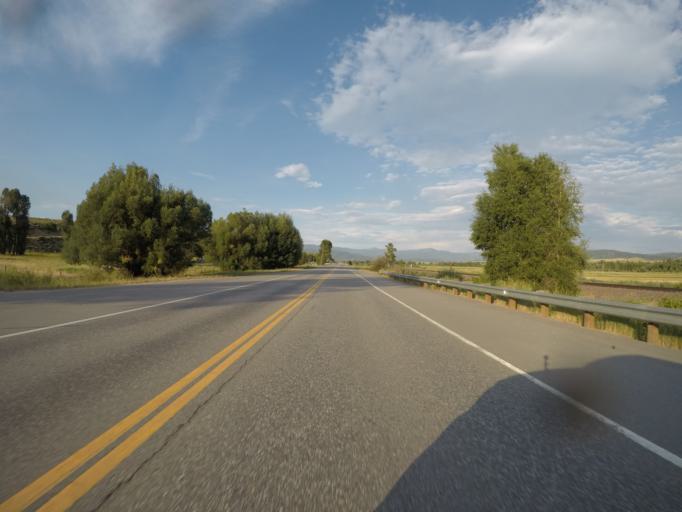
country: US
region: Colorado
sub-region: Routt County
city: Steamboat Springs
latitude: 40.4874
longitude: -106.9672
